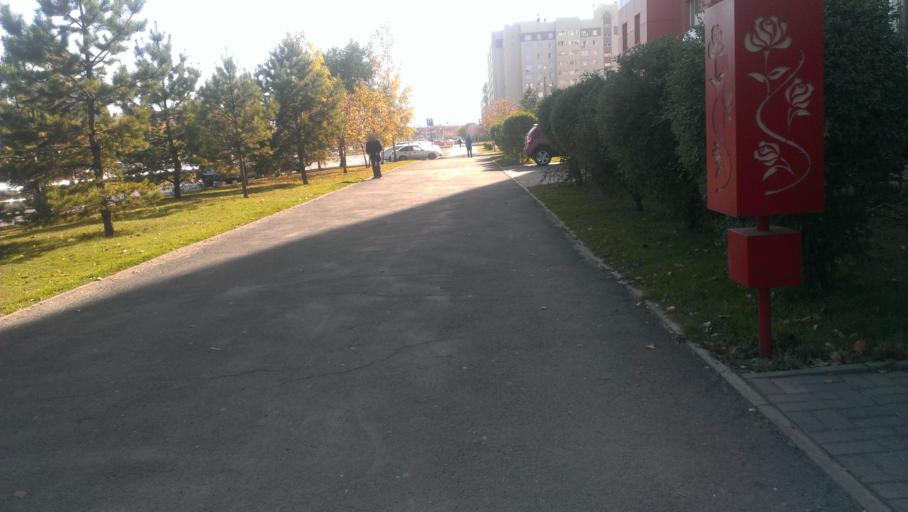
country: RU
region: Altai Krai
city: Novosilikatnyy
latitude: 53.3350
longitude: 83.6930
